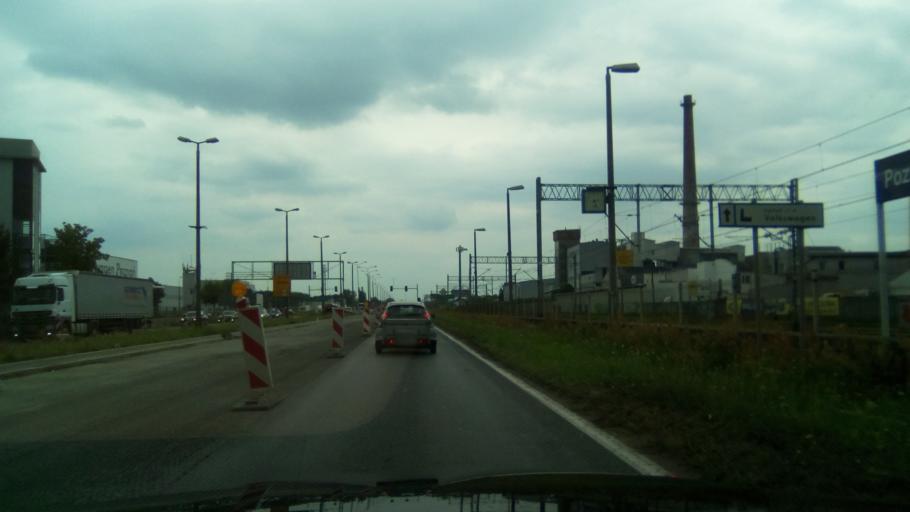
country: PL
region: Greater Poland Voivodeship
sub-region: Powiat poznanski
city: Swarzedz
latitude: 52.4090
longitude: 17.0309
